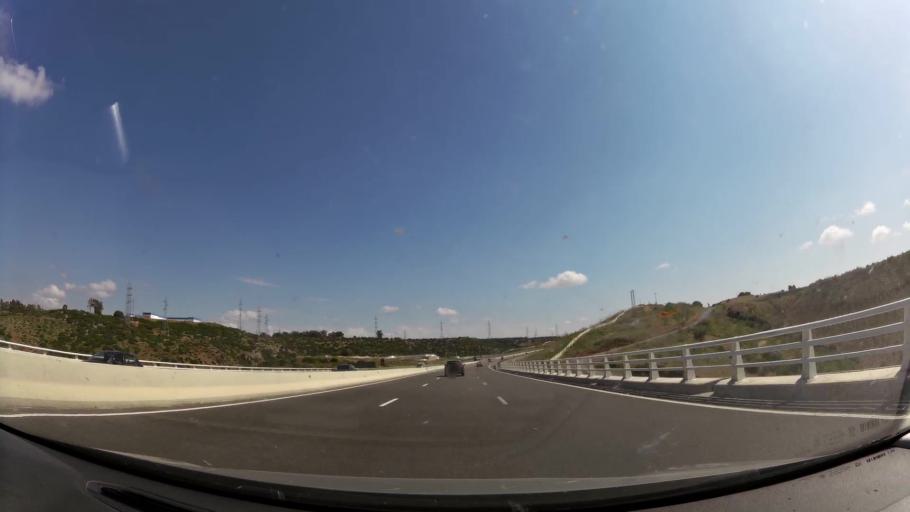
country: MA
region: Rabat-Sale-Zemmour-Zaer
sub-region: Rabat
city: Rabat
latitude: 33.9342
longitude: -6.7602
